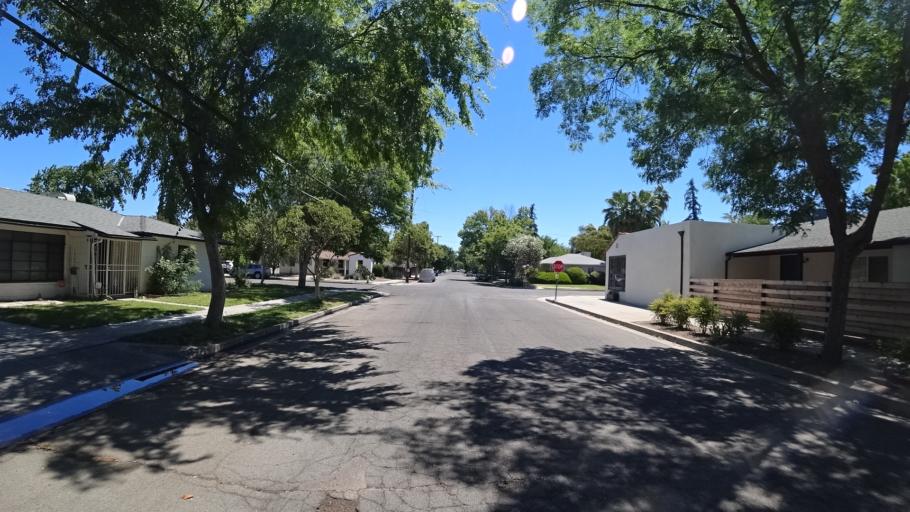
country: US
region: California
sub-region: Fresno County
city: Fresno
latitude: 36.7775
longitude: -119.8134
